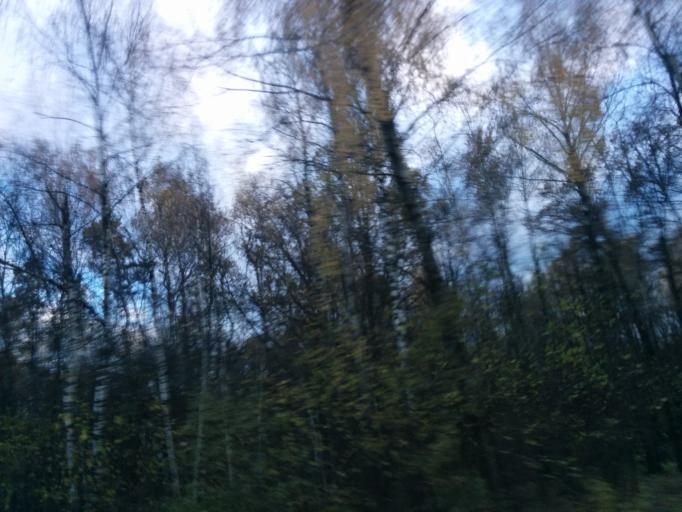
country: RU
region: Moscow
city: Annino
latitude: 55.5443
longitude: 37.6125
